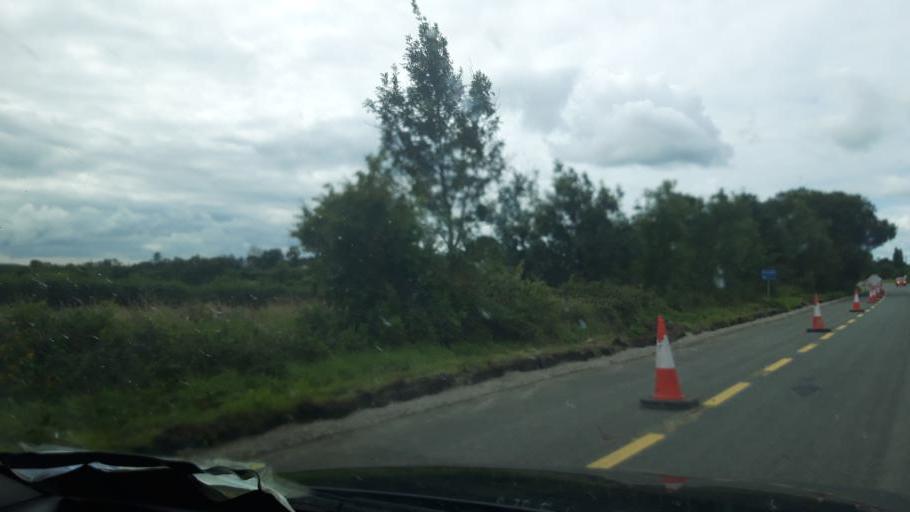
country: IE
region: Leinster
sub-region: Kilkenny
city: Kilkenny
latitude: 52.6088
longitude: -7.2952
